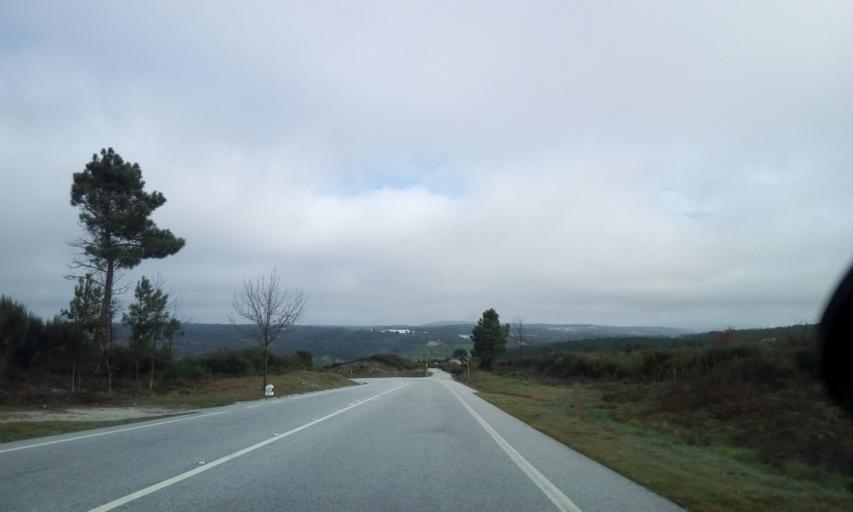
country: PT
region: Guarda
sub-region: Aguiar da Beira
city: Aguiar da Beira
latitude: 40.7697
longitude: -7.5034
